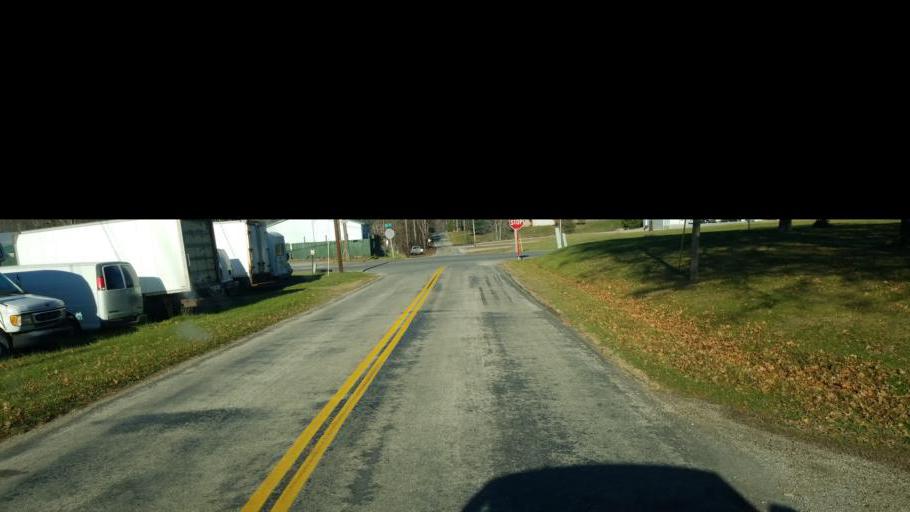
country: US
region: Ohio
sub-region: Ashland County
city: Ashland
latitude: 40.8382
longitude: -82.3637
